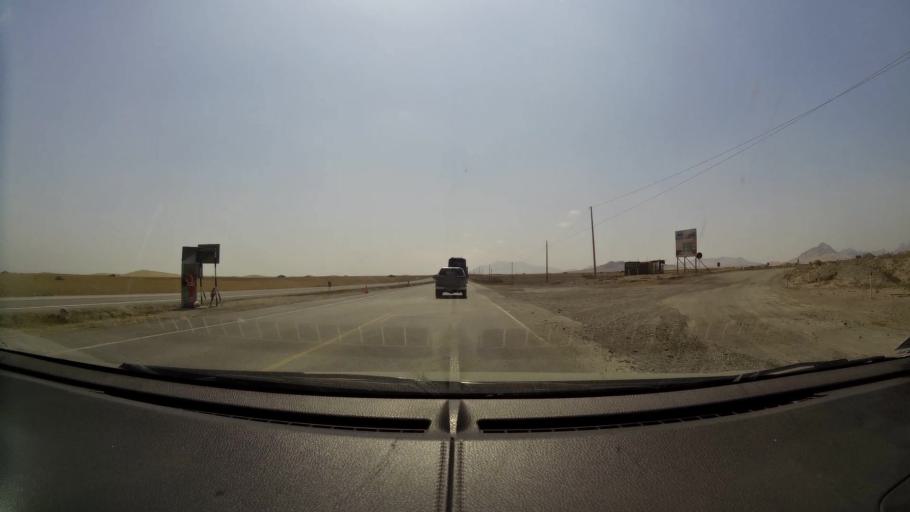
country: PE
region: Lambayeque
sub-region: Provincia de Chiclayo
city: Mocupe
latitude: -6.9701
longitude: -79.6776
